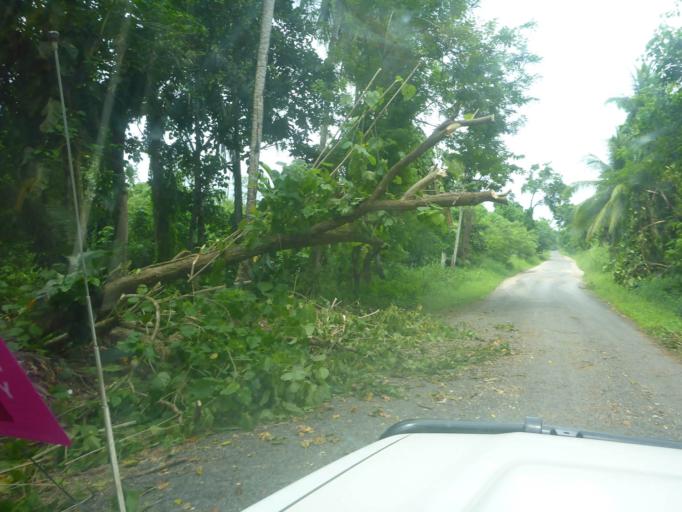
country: PG
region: Madang
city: Madang
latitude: -4.6774
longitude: 145.5921
